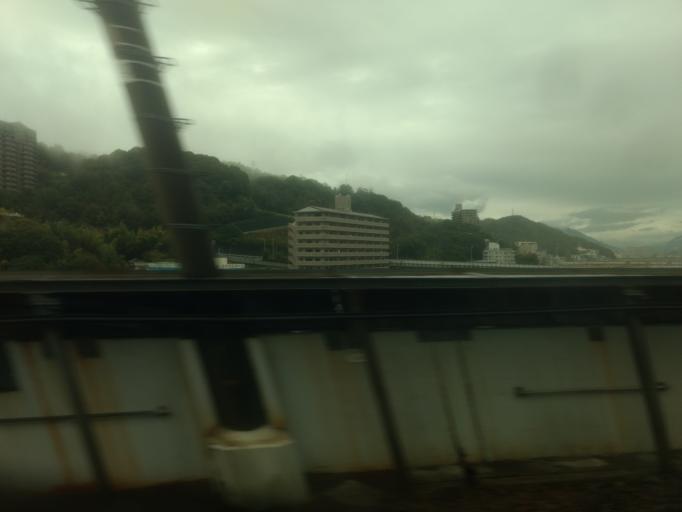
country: JP
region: Hiroshima
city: Hiroshima-shi
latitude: 34.4092
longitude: 132.4426
